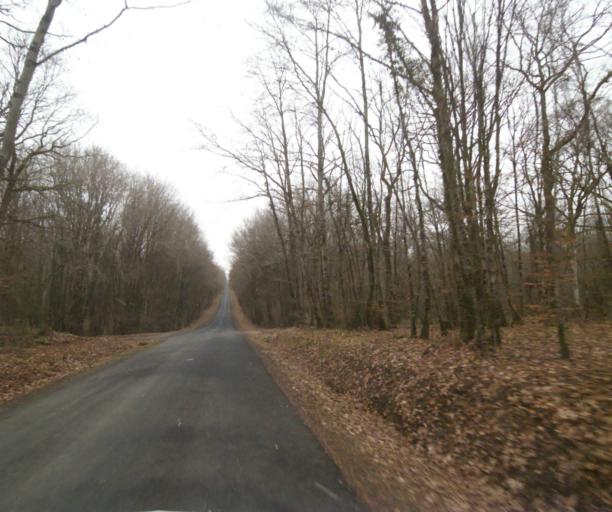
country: FR
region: Champagne-Ardenne
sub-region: Departement de la Haute-Marne
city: Bienville
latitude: 48.5571
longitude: 5.0029
